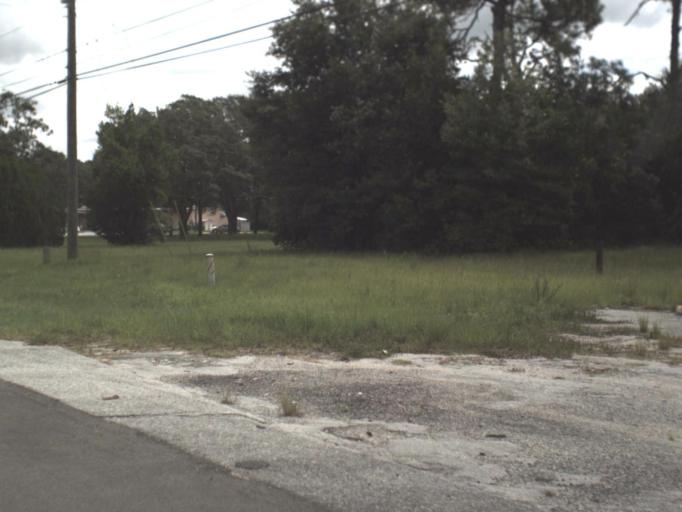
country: US
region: Florida
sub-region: Hernando County
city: Masaryktown
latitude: 28.4300
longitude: -82.4639
